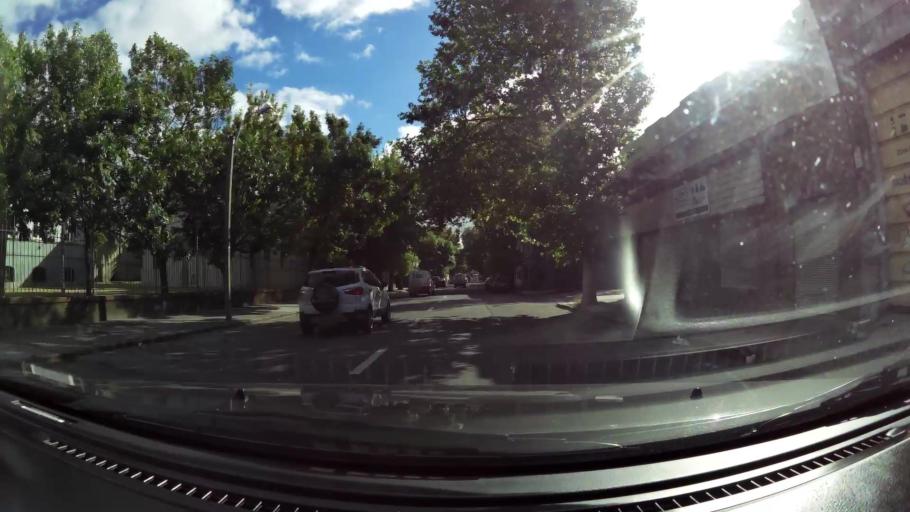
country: UY
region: Montevideo
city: Montevideo
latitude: -34.8947
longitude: -56.1798
